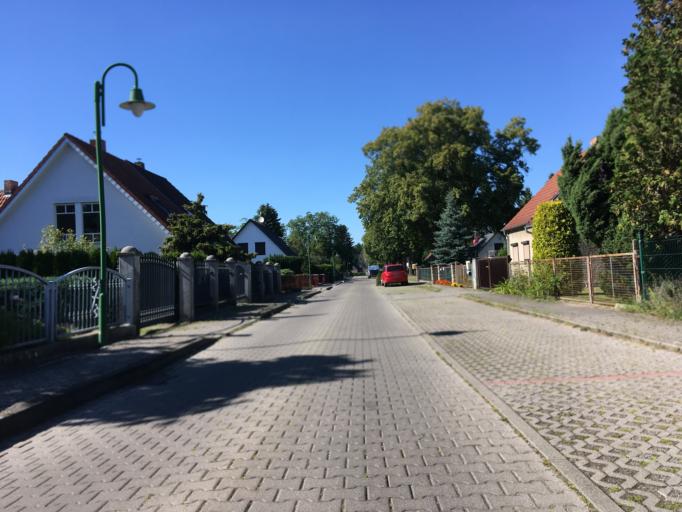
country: DE
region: Brandenburg
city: Schulzendorf
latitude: 52.3809
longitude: 13.5911
